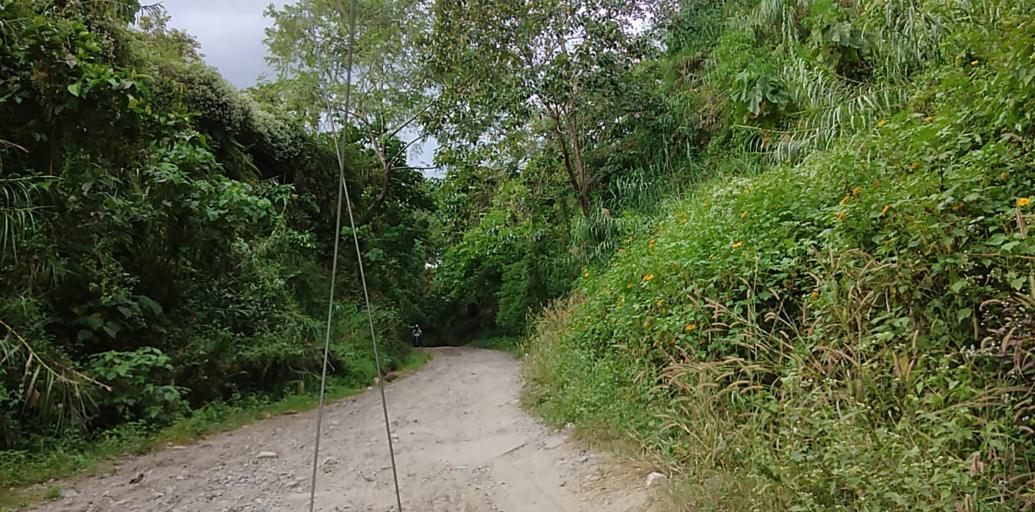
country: PH
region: Central Luzon
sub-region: Province of Pampanga
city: Babo-Pangulo
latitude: 15.1112
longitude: 120.4977
